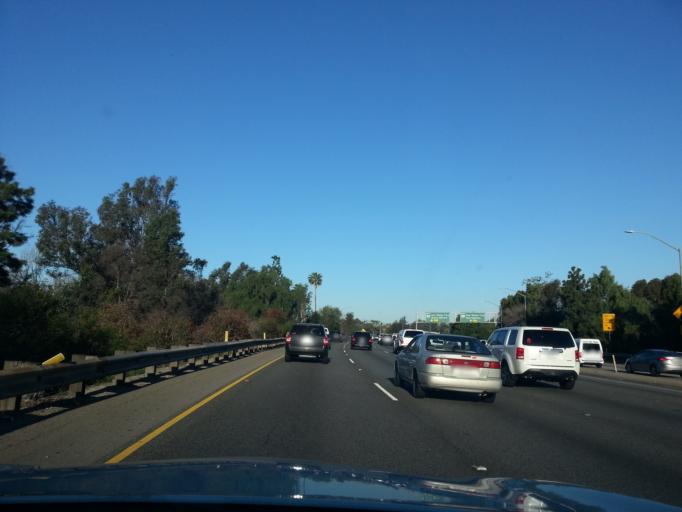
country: US
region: California
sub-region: Los Angeles County
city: Sherman Oaks
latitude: 34.1598
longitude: -118.4667
